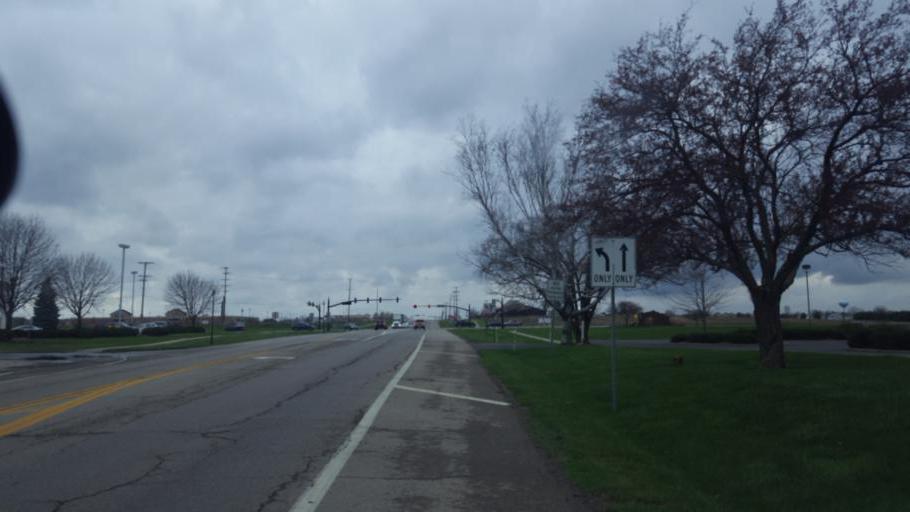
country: US
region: Ohio
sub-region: Delaware County
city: Sunbury
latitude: 40.2447
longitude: -82.8634
